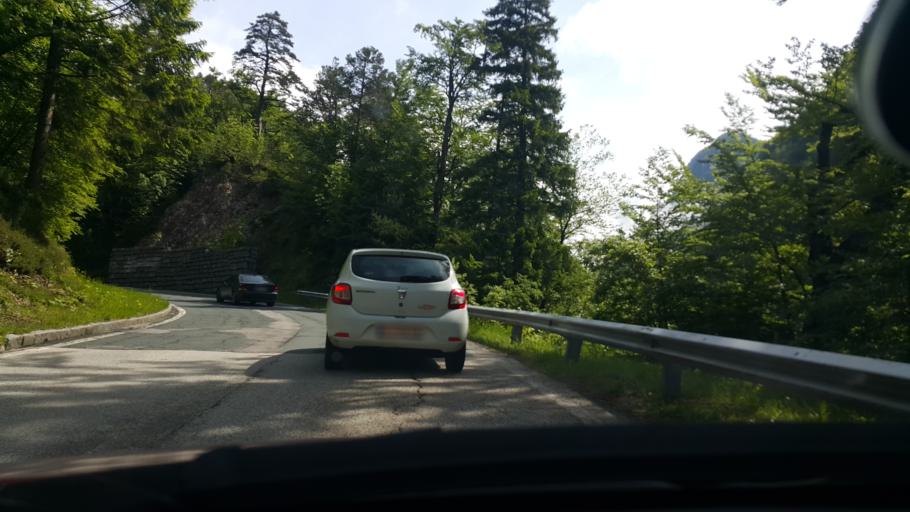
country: AT
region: Carinthia
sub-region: Politischer Bezirk Klagenfurt Land
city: Ferlach
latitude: 46.4844
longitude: 14.2632
